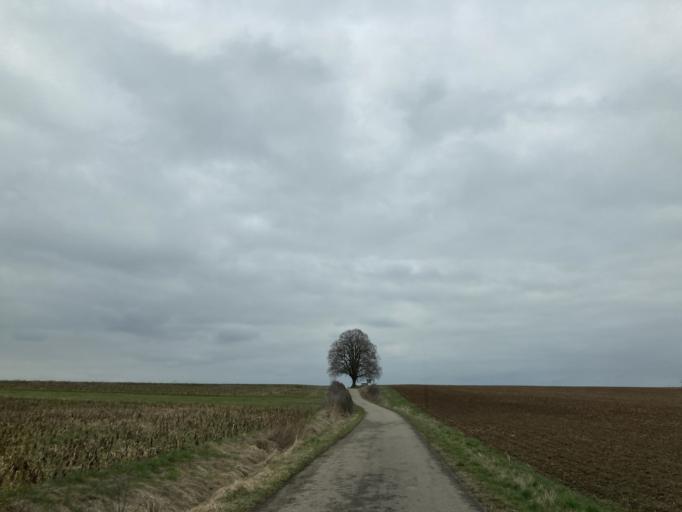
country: DE
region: Baden-Wuerttemberg
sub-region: Tuebingen Region
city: Hirrlingen
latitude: 48.4216
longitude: 8.8976
